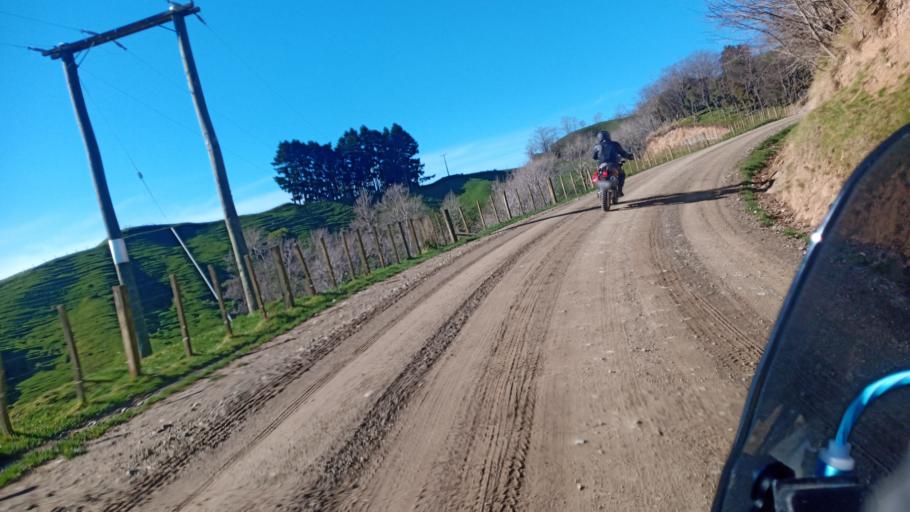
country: NZ
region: Gisborne
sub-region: Gisborne District
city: Gisborne
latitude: -38.2920
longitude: 177.8831
